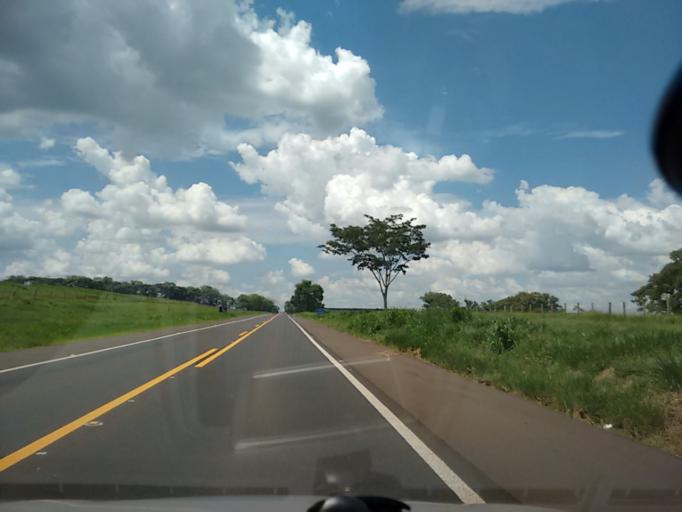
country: BR
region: Sao Paulo
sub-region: Osvaldo Cruz
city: Osvaldo Cruz
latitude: -21.8790
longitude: -50.8626
